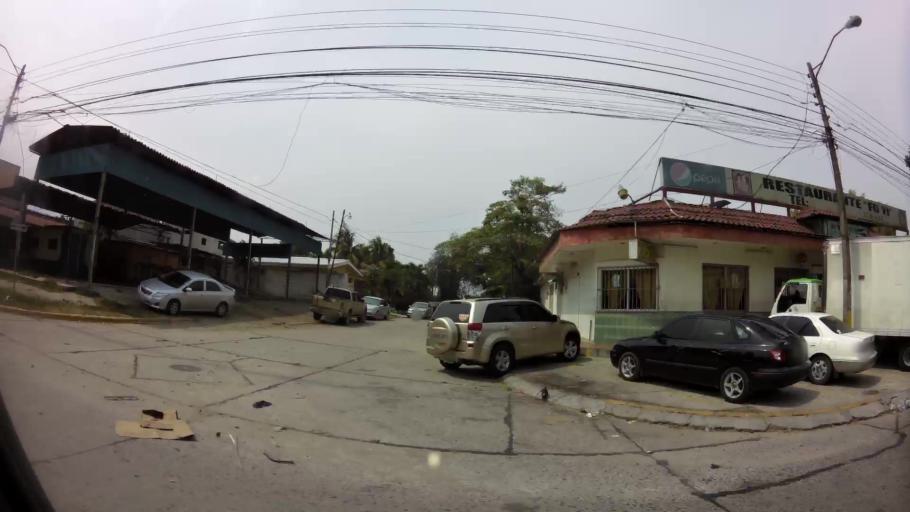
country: HN
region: Cortes
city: San Pedro Sula
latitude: 15.5178
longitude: -88.0190
